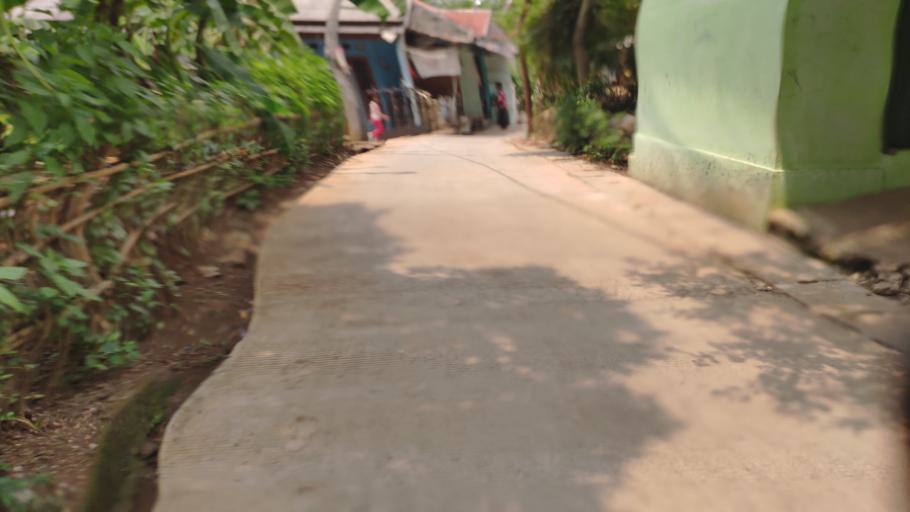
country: ID
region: West Java
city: Sawangan
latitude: -6.3882
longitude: 106.7895
